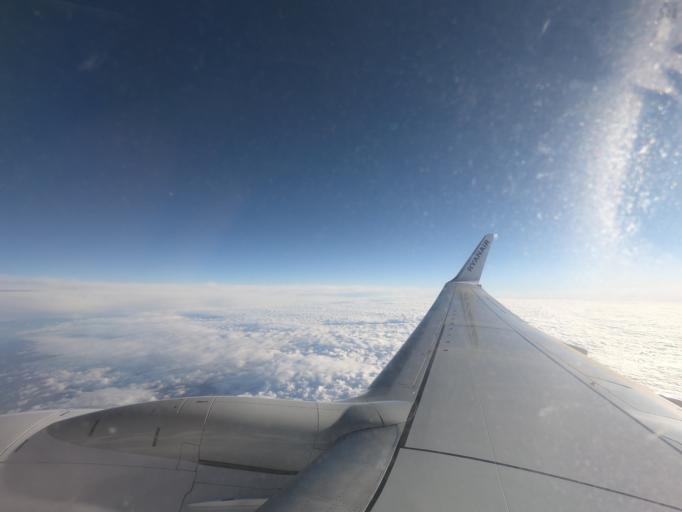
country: DE
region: Rheinland-Pfalz
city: Bretzenheim
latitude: 49.8778
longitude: 7.9013
